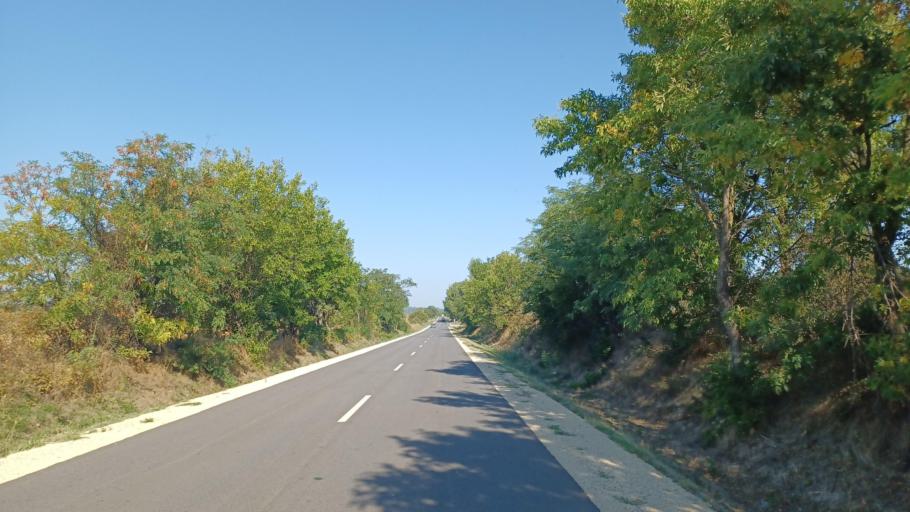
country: HU
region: Tolna
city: Paks
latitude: 46.6533
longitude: 18.8377
